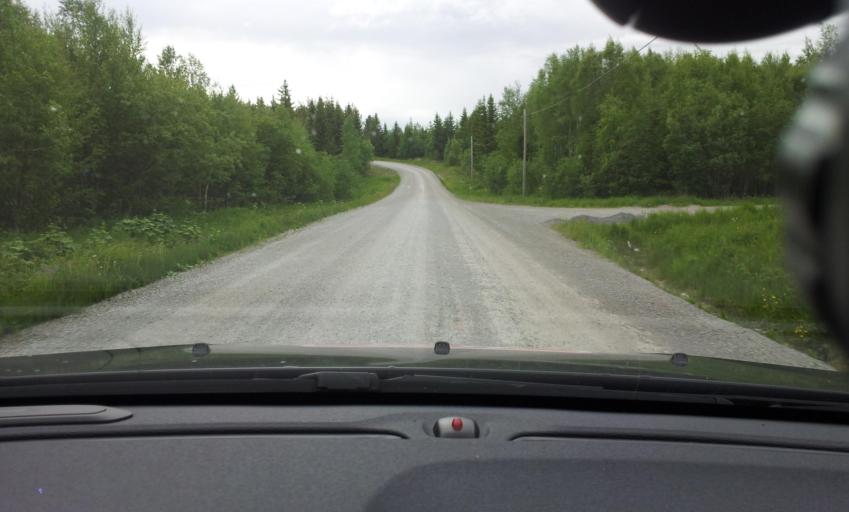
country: SE
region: Jaemtland
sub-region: OEstersunds Kommun
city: Brunflo
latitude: 63.0914
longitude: 14.8938
